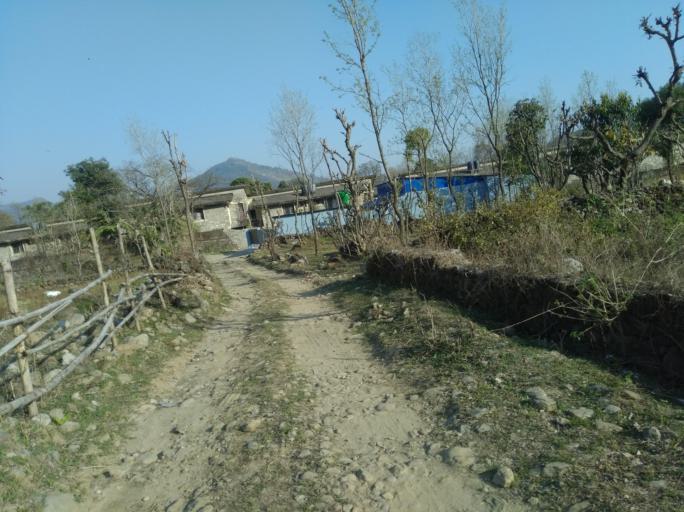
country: NP
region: Western Region
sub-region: Gandaki Zone
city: Pokhara
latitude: 28.2546
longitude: 83.9731
